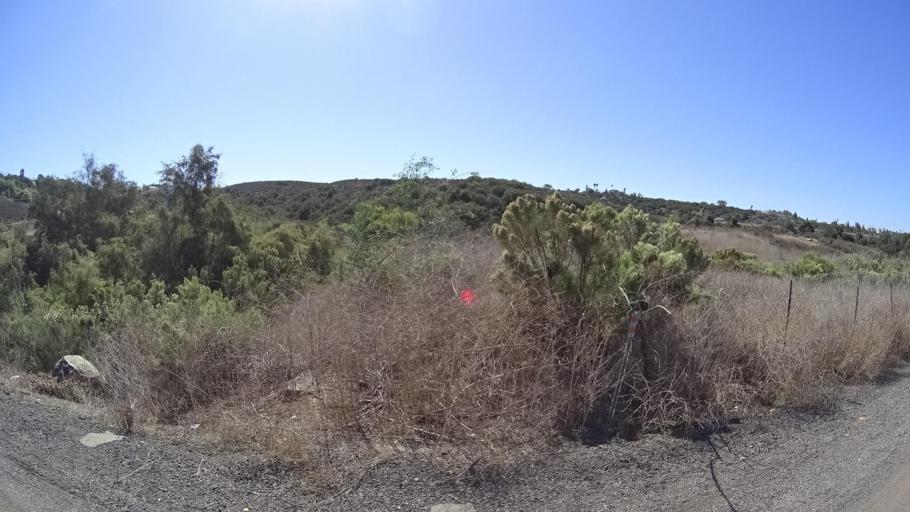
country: US
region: California
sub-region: San Diego County
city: La Presa
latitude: 32.6661
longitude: -116.9819
